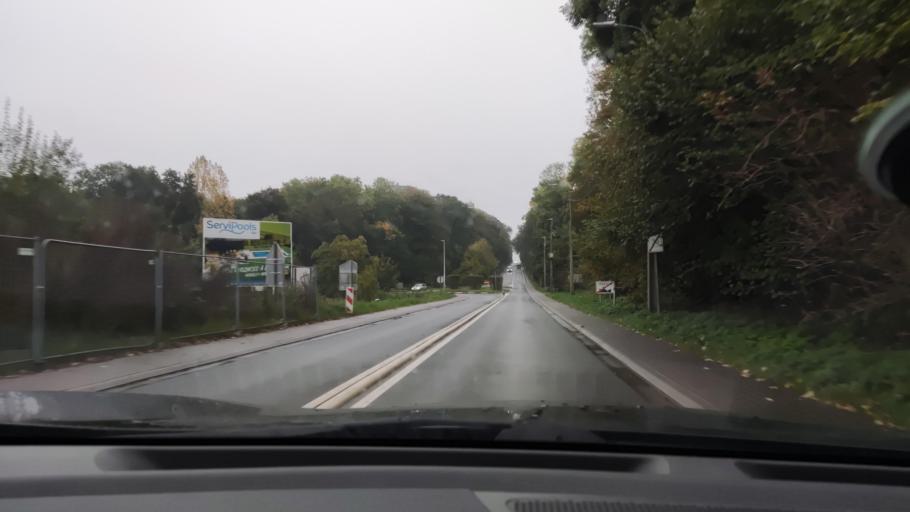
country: BE
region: Wallonia
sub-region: Province du Brabant Wallon
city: Jodoigne
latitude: 50.7185
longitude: 4.8833
